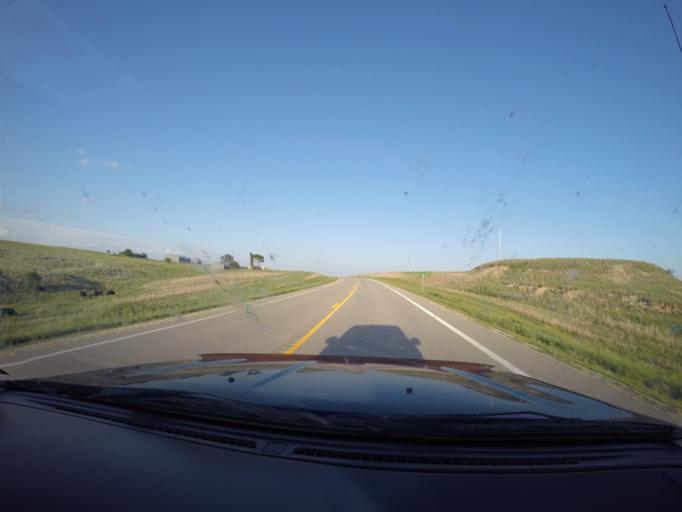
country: US
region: Kansas
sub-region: Marshall County
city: Blue Rapids
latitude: 39.6974
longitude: -96.8504
